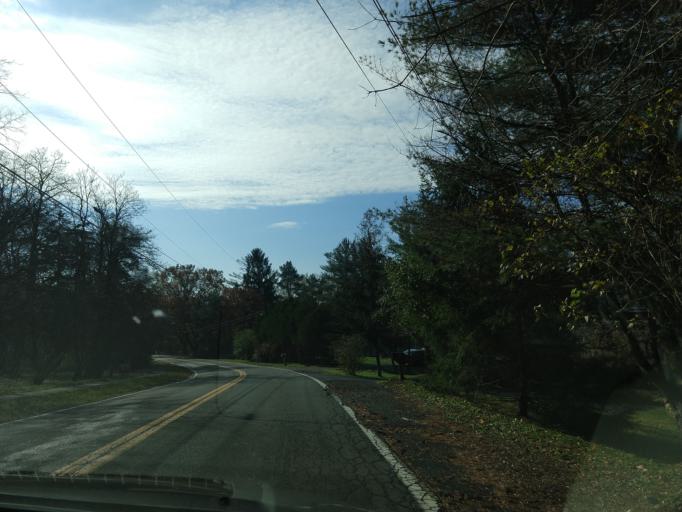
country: US
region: New York
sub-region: Tompkins County
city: Cayuga Heights
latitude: 42.4664
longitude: -76.4823
